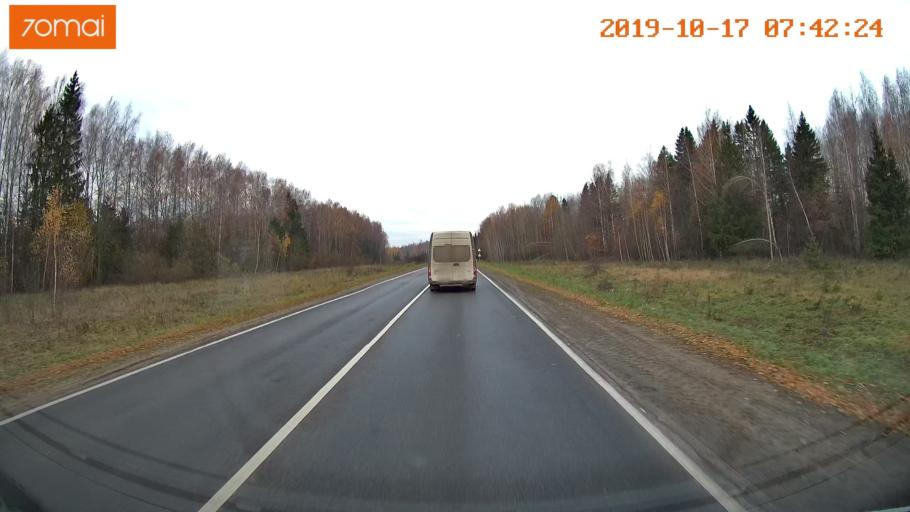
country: RU
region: Vladimir
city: Yur'yev-Pol'skiy
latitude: 56.4843
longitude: 39.7882
